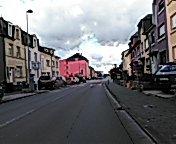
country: LU
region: Luxembourg
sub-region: Canton d'Esch-sur-Alzette
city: Esch-sur-Alzette
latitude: 49.5058
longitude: 5.9694
